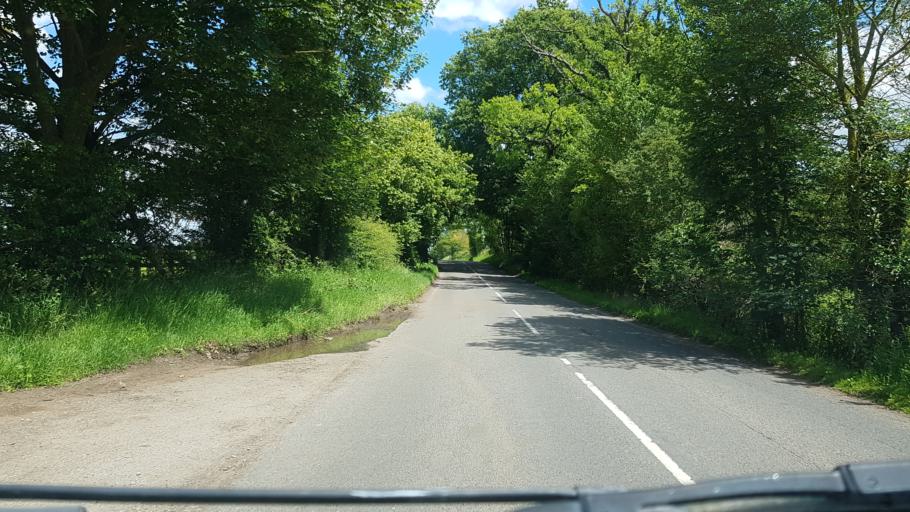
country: GB
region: England
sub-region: Warwickshire
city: Stratford-upon-Avon
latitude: 52.2324
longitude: -1.6830
